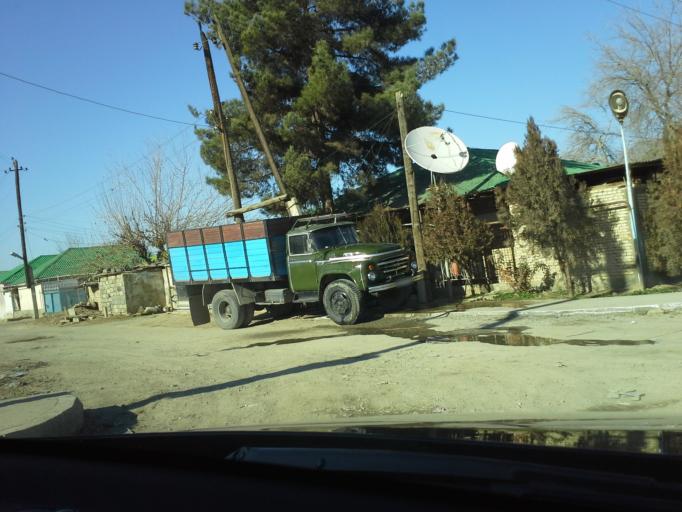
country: TM
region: Ahal
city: Ashgabat
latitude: 37.9611
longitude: 58.3386
